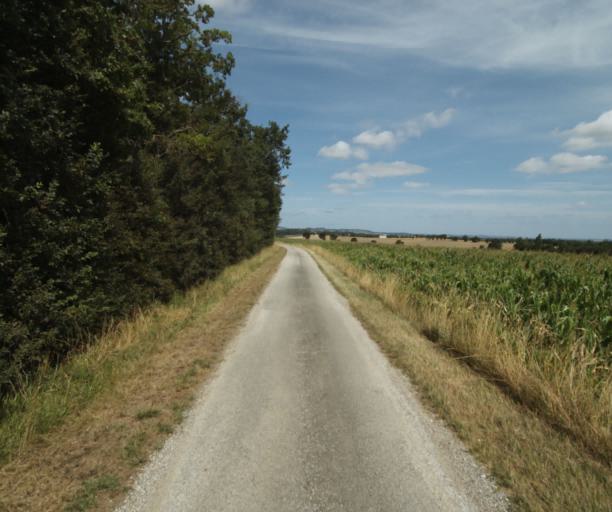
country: FR
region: Midi-Pyrenees
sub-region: Departement du Tarn
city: Dourgne
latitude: 43.4871
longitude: 2.1011
